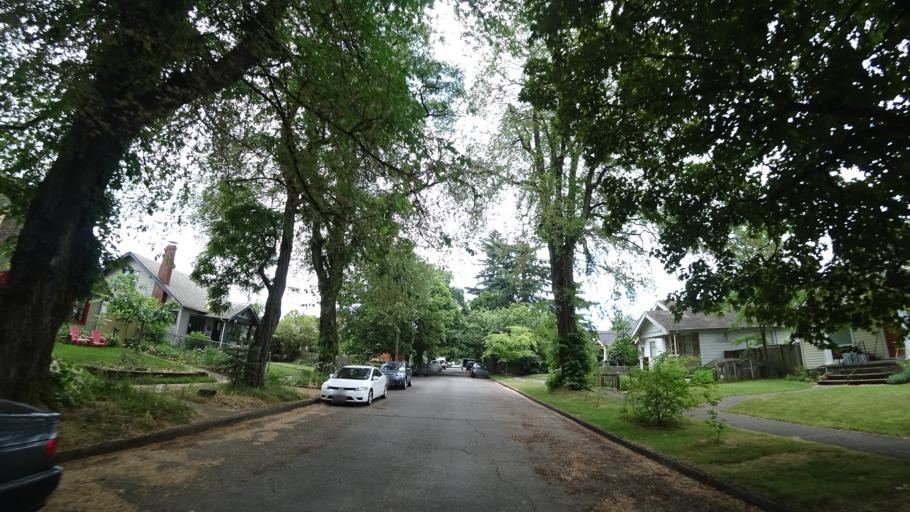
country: US
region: Oregon
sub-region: Multnomah County
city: Portland
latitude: 45.5688
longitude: -122.6702
